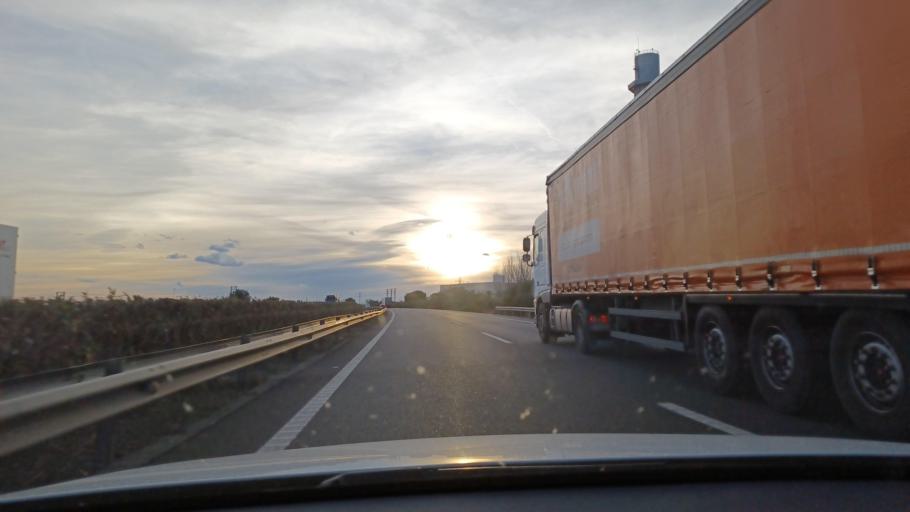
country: ES
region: Catalonia
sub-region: Provincia de Tarragona
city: Camarles
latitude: 40.8006
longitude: 0.6775
